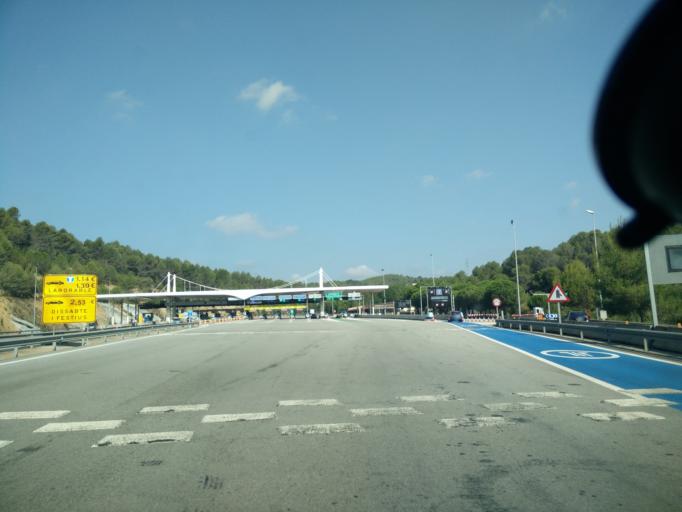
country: ES
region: Catalonia
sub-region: Provincia de Barcelona
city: Rubi
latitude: 41.5172
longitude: 2.0322
